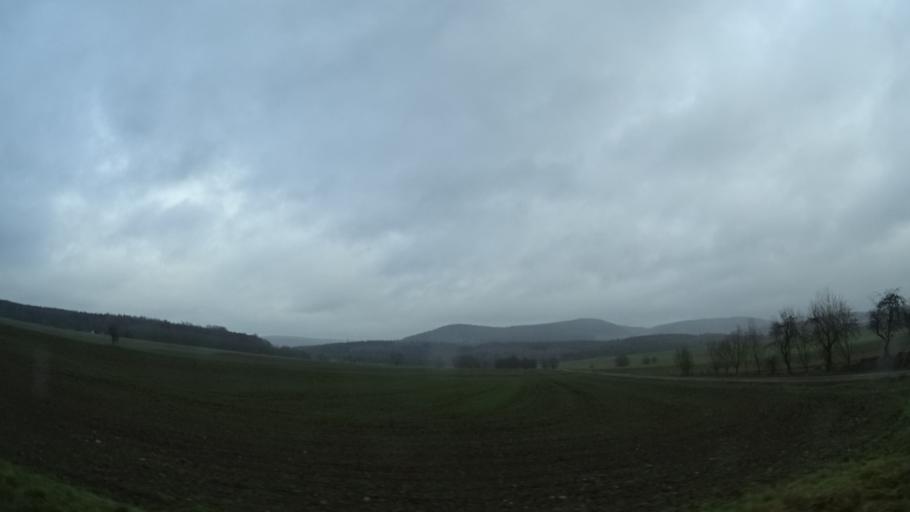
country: DE
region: Thuringia
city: Wolfershausen
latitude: 50.4725
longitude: 10.4252
